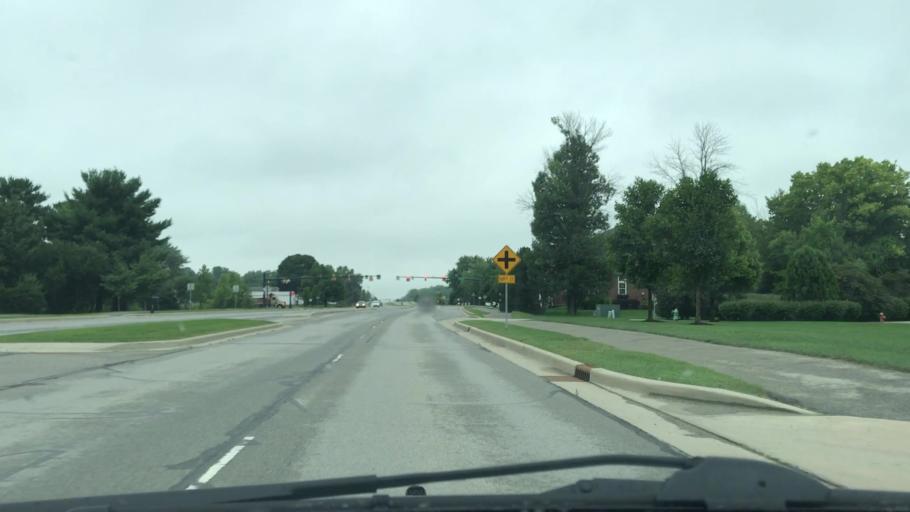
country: US
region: Indiana
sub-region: Hamilton County
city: Westfield
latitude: 40.0314
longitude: -86.0706
